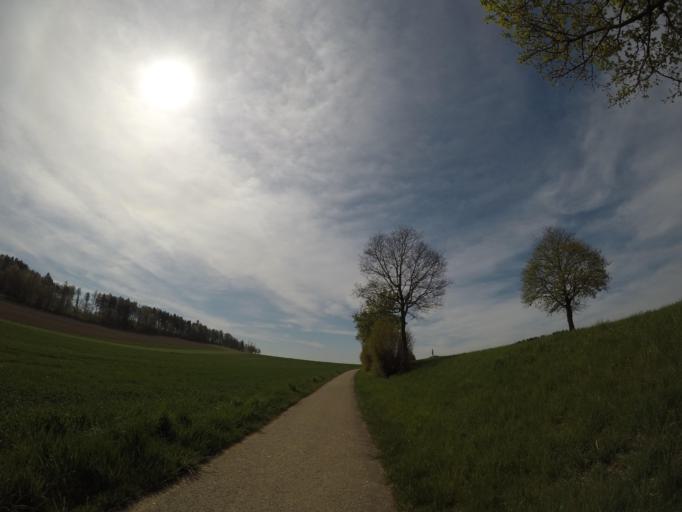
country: DE
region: Baden-Wuerttemberg
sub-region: Tuebingen Region
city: Boms
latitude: 47.9872
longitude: 9.5161
